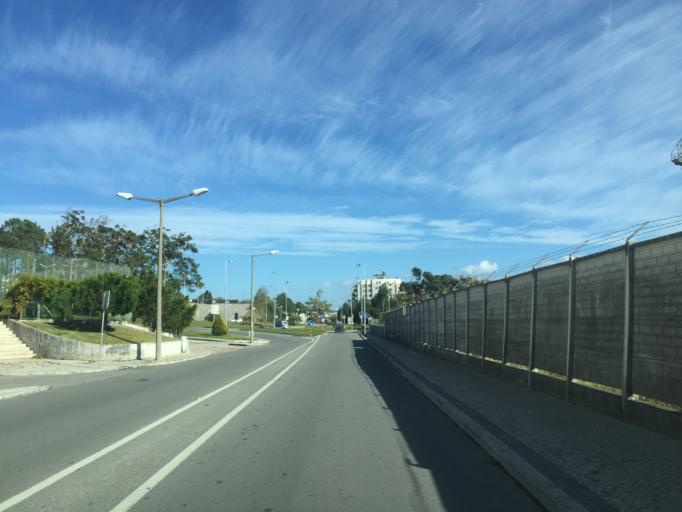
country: PT
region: Coimbra
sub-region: Figueira da Foz
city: Figueira da Foz
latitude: 40.1637
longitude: -8.8599
